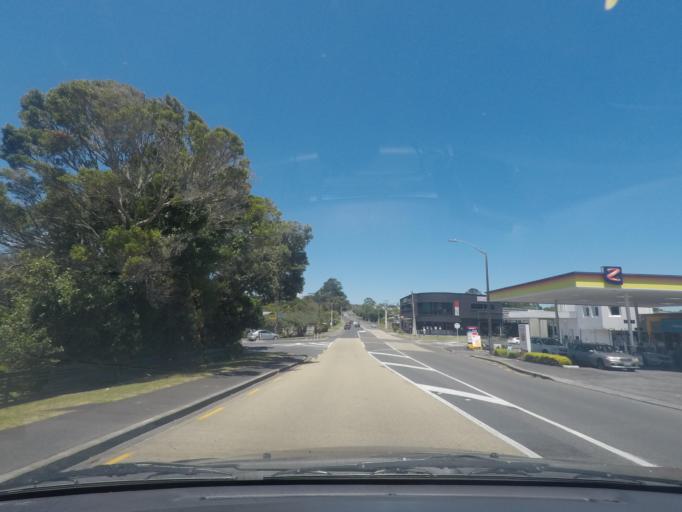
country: NZ
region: Auckland
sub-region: Auckland
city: Waitakere
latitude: -36.9221
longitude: 174.7195
